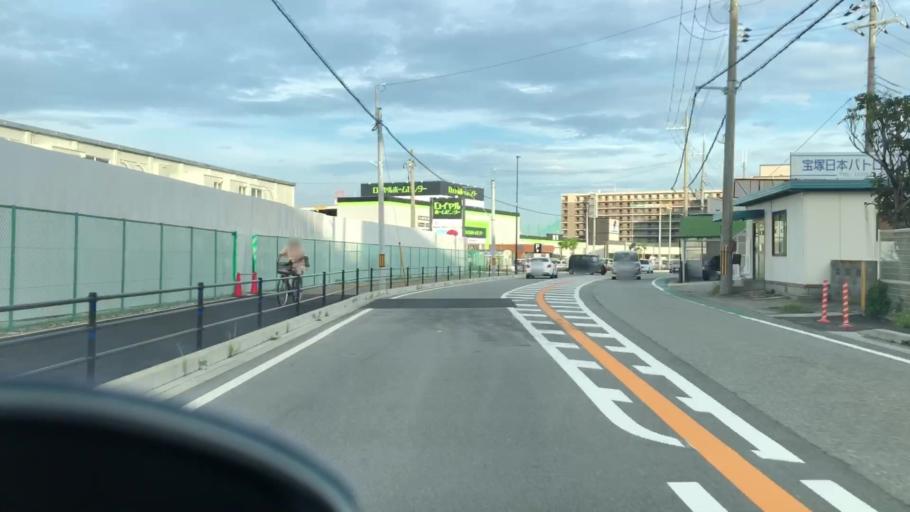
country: JP
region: Hyogo
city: Takarazuka
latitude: 34.7977
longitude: 135.3618
